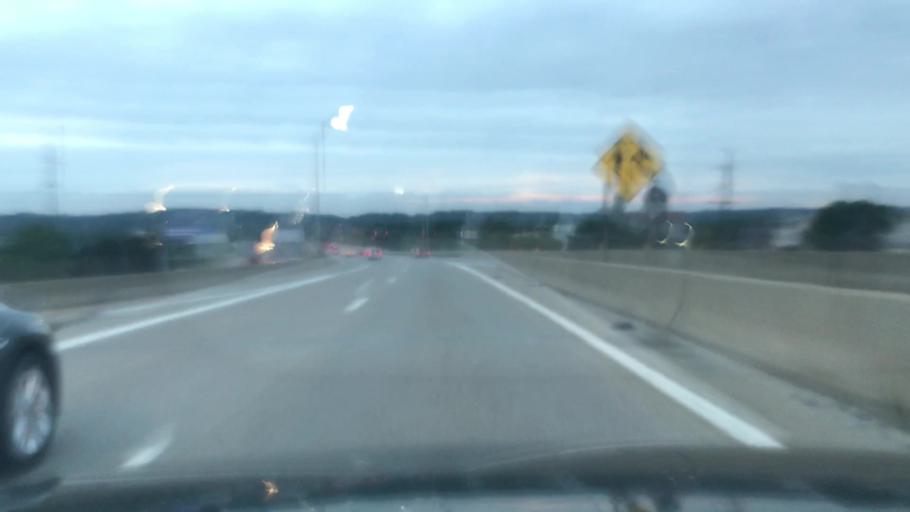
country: US
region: Michigan
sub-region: Kent County
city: Grand Rapids
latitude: 42.9733
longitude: -85.6790
